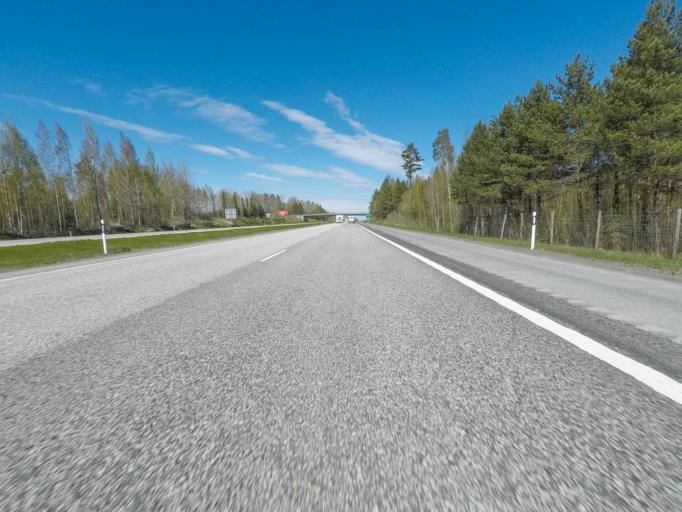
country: FI
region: Haeme
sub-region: Riihimaeki
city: Riihimaeki
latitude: 60.7014
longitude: 24.7400
